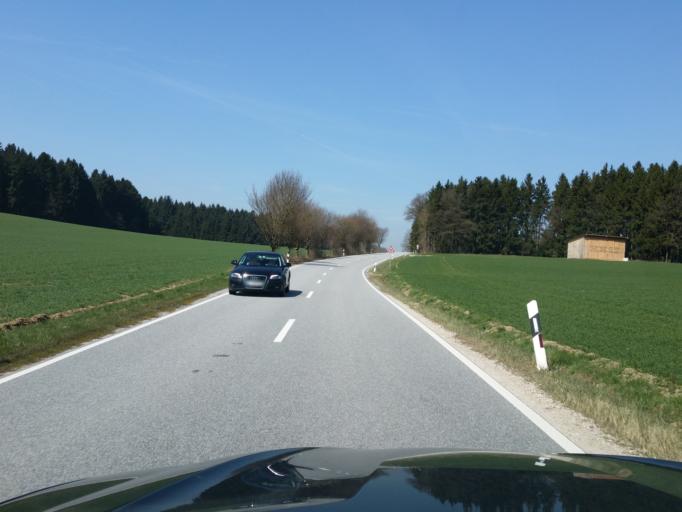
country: DE
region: Bavaria
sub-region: Upper Bavaria
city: Kirchberg
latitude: 48.4428
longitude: 12.0604
